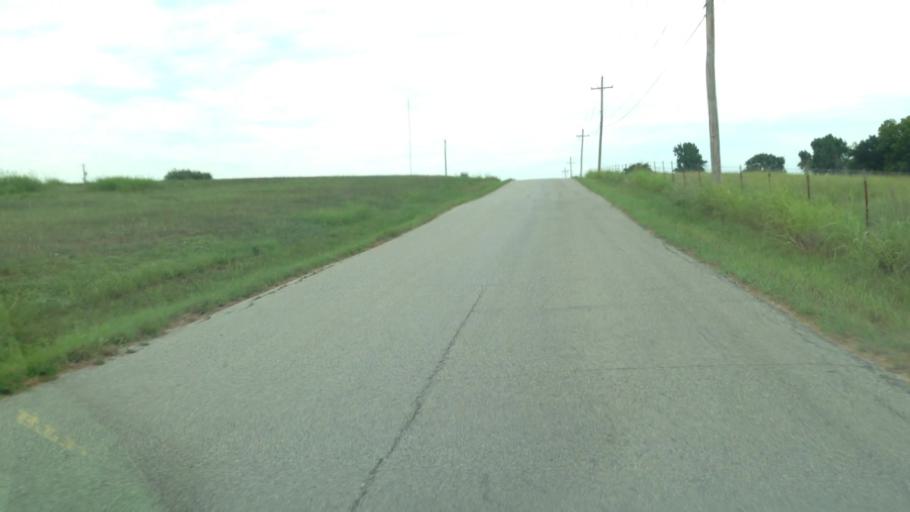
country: US
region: Oklahoma
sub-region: Craig County
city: Vinita
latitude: 36.6418
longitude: -95.1255
